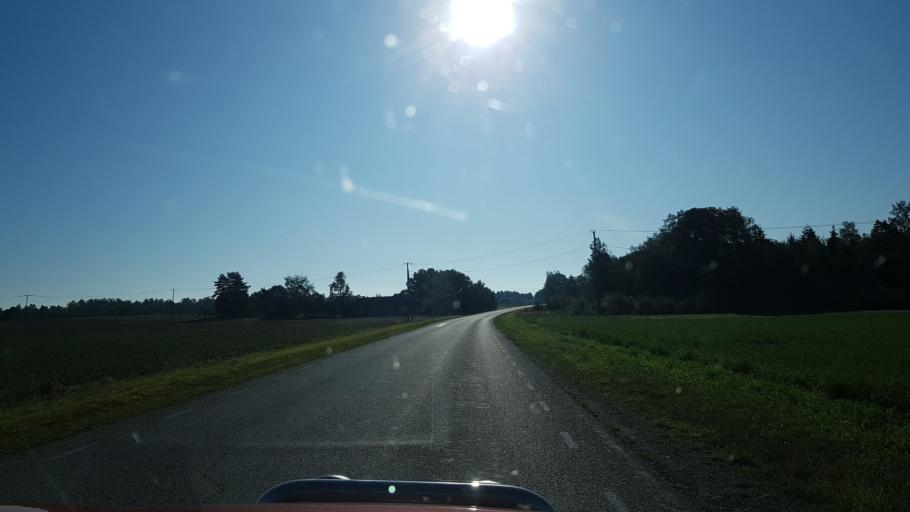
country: EE
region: Jogevamaa
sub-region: Tabivere vald
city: Tabivere
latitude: 58.6836
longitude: 26.6095
